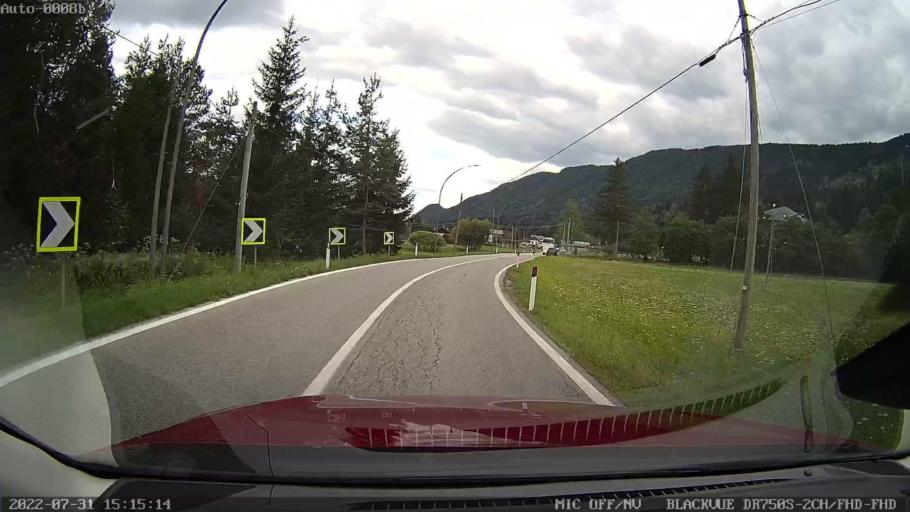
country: AT
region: Carinthia
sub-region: Politischer Bezirk Villach Land
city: Arnoldstein
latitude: 46.4976
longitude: 13.6966
